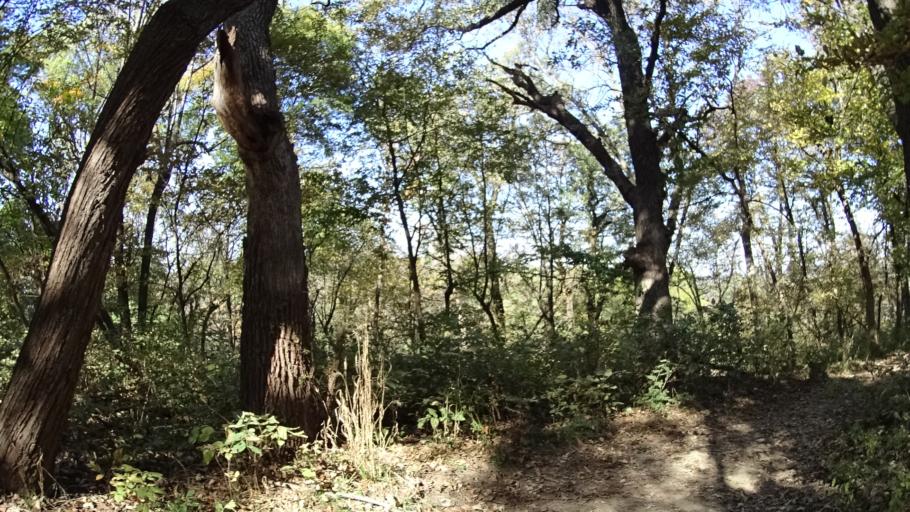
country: US
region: Nebraska
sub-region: Sarpy County
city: Bellevue
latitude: 41.1804
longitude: -95.9146
